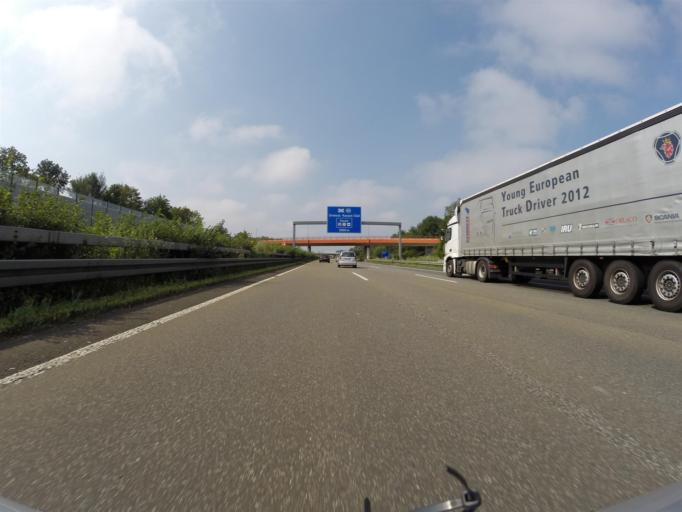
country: DE
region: Hesse
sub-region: Regierungsbezirk Kassel
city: Lohfelden
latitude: 51.2786
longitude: 9.5338
